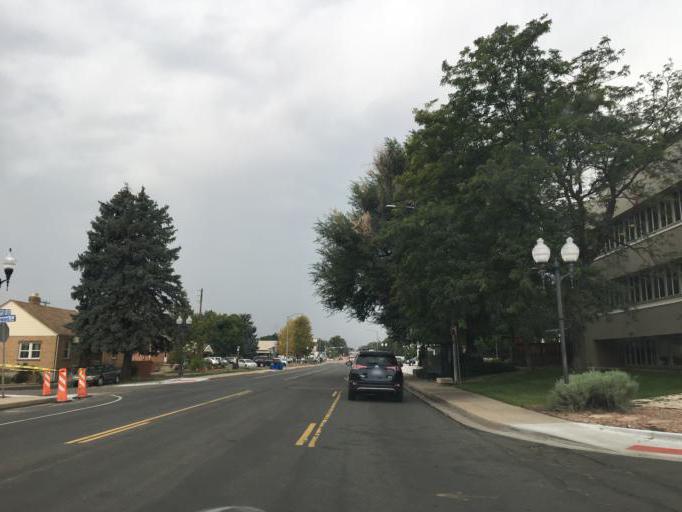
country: US
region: Colorado
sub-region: Jefferson County
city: Wheat Ridge
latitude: 39.7694
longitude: -105.0686
